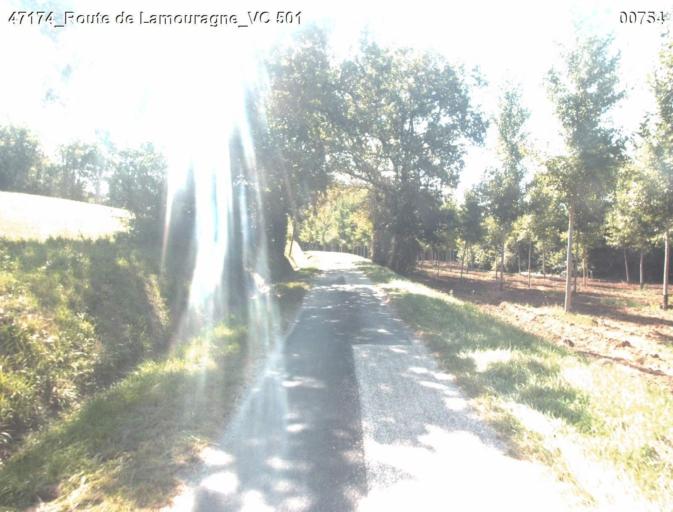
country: FR
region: Midi-Pyrenees
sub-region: Departement du Gers
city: Condom
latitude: 44.0410
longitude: 0.3868
